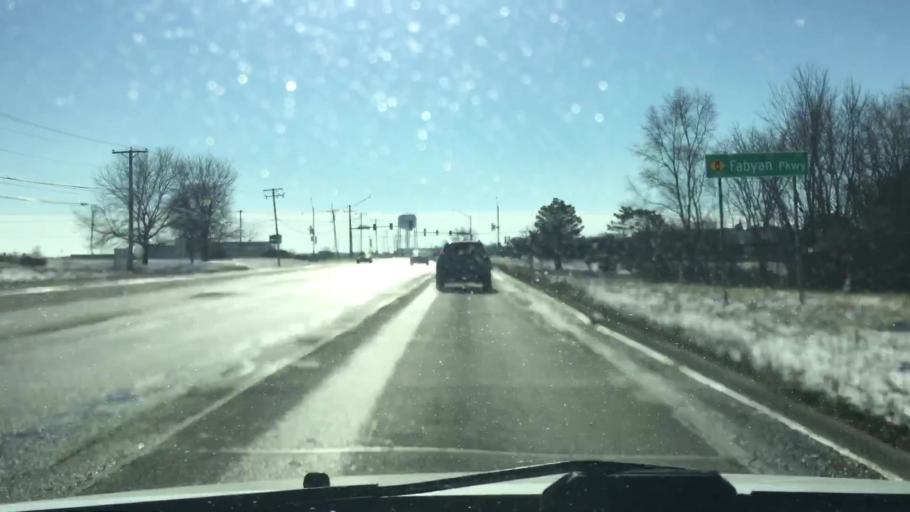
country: US
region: Illinois
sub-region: Kane County
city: Geneva
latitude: 41.8707
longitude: -88.2791
